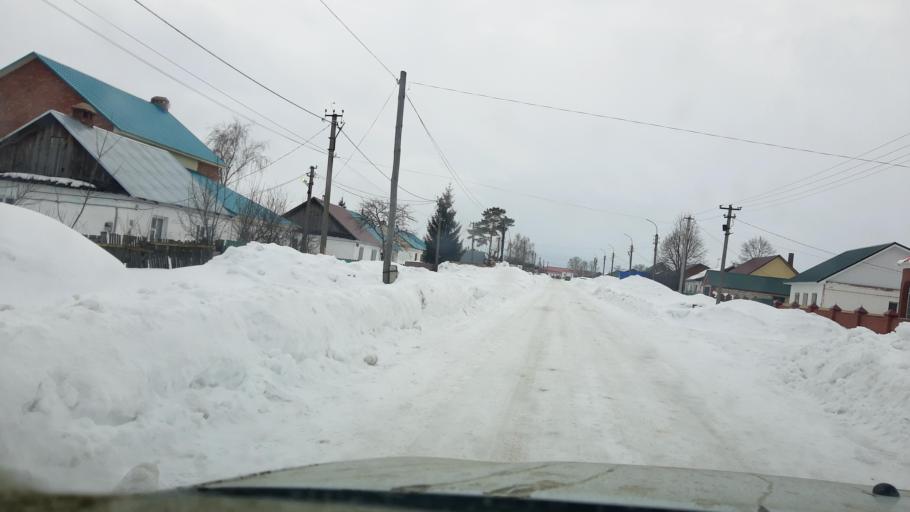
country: RU
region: Bashkortostan
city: Karmaskaly
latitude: 54.4165
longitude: 56.1631
